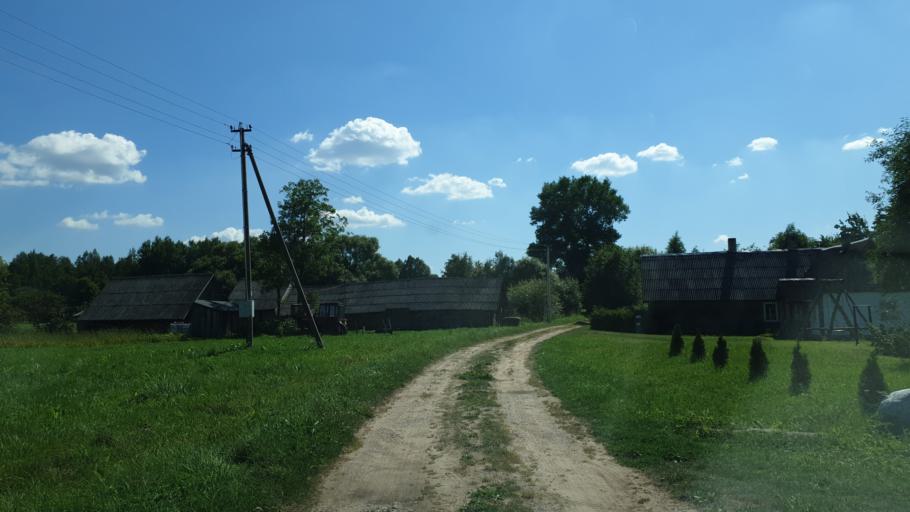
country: LT
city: Sirvintos
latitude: 54.9030
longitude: 24.9111
